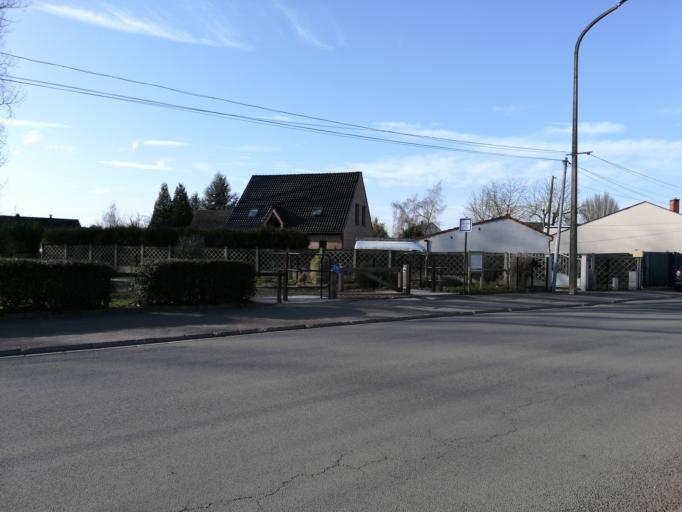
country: FR
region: Nord-Pas-de-Calais
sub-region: Departement du Pas-de-Calais
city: Henin-Beaumont
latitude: 50.4078
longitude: 2.9548
